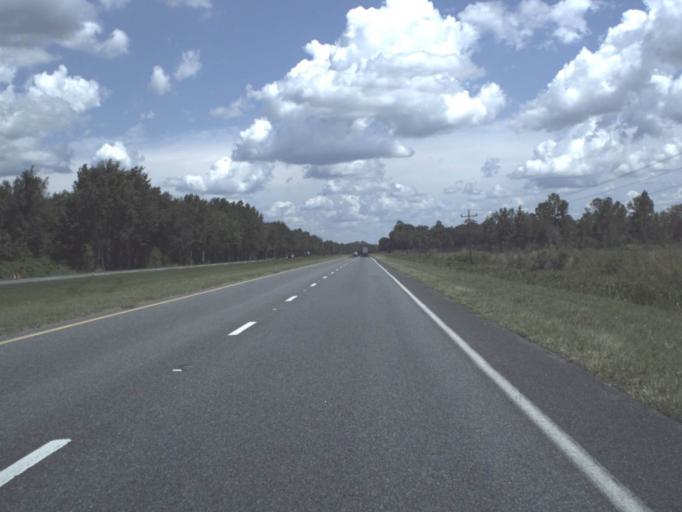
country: US
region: Florida
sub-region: Taylor County
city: Steinhatchee
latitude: 29.8267
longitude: -83.3580
